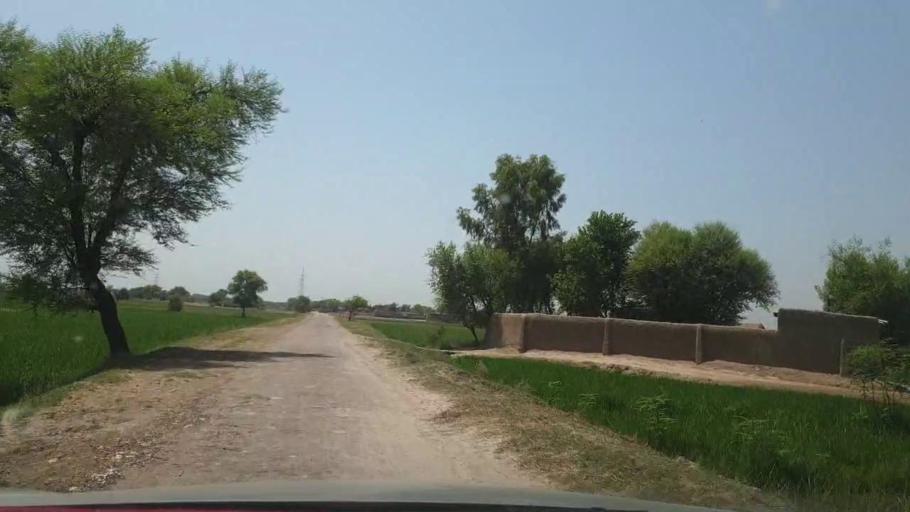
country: PK
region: Sindh
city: Warah
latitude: 27.4977
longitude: 67.7517
